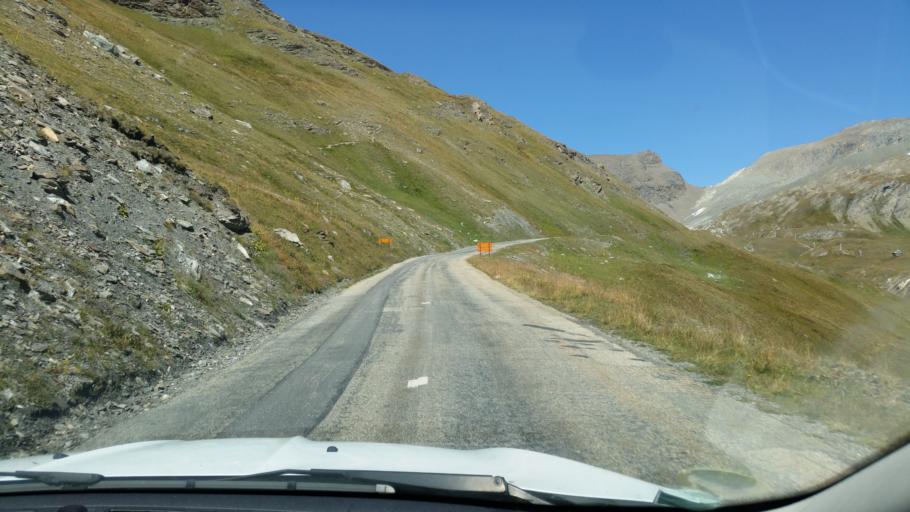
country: FR
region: Rhone-Alpes
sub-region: Departement de la Savoie
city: Val-d'Isere
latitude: 45.4119
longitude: 7.0294
